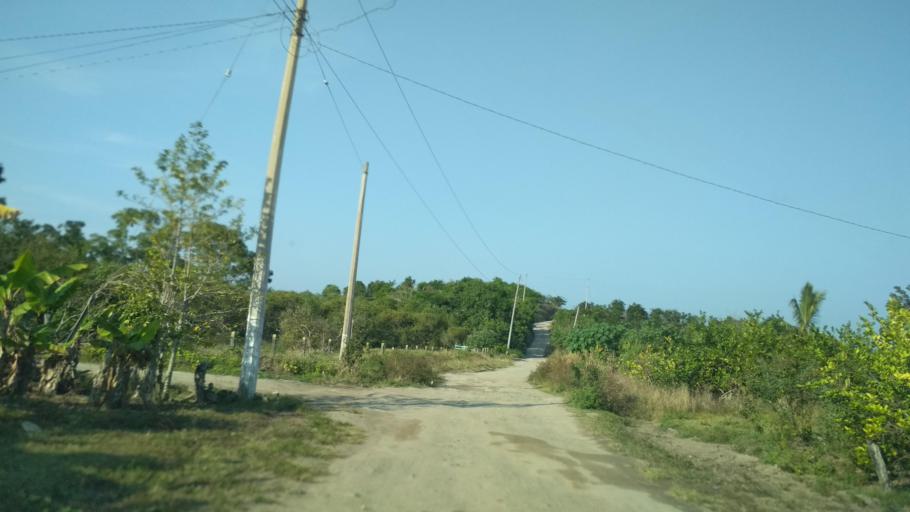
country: MX
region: Puebla
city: San Jose Acateno
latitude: 20.2206
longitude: -97.2622
